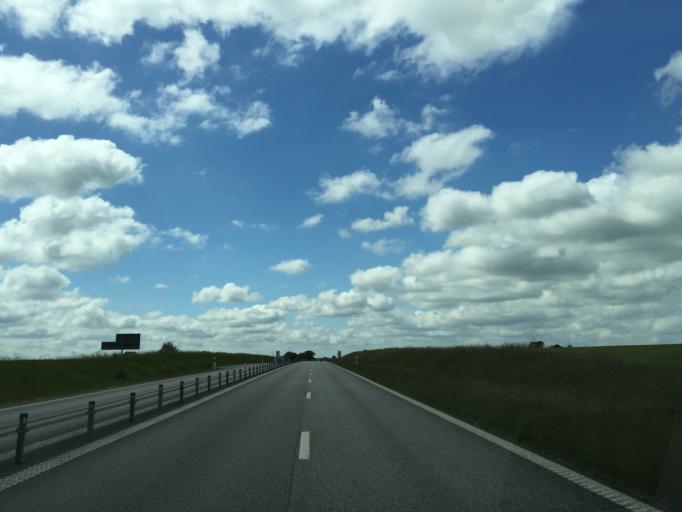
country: SE
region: Skane
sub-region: Skurups Kommun
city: Rydsgard
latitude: 55.4767
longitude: 13.6428
